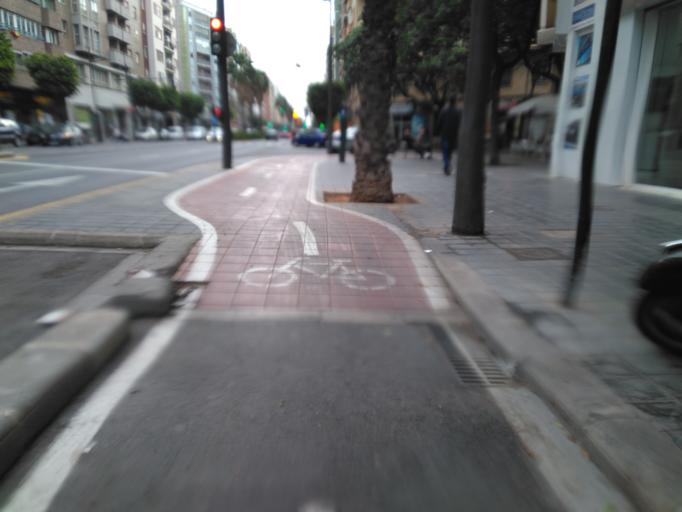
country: ES
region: Valencia
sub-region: Provincia de Valencia
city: Valencia
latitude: 39.4621
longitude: -0.3637
